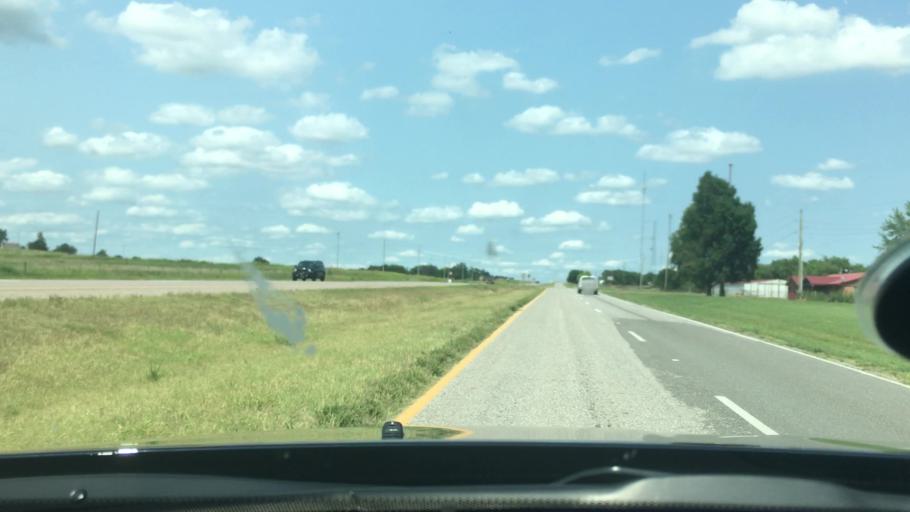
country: US
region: Oklahoma
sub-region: Pontotoc County
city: Ada
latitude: 34.6784
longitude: -96.7710
